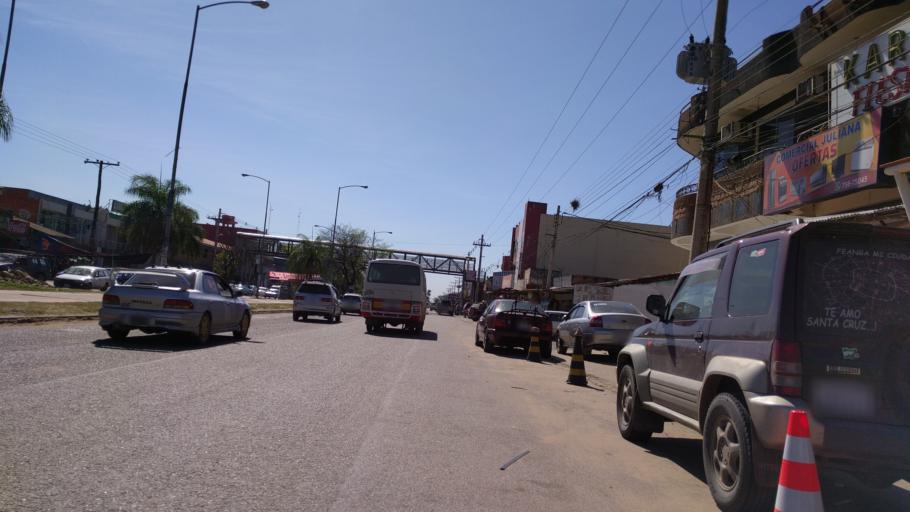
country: BO
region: Santa Cruz
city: Santa Cruz de la Sierra
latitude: -17.8291
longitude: -63.2275
